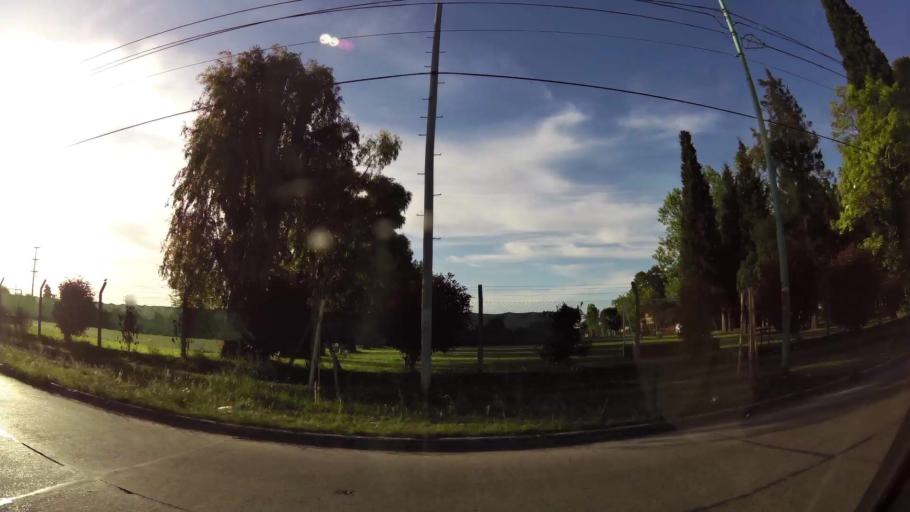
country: AR
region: Buenos Aires
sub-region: Partido de Quilmes
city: Quilmes
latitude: -34.7892
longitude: -58.2163
